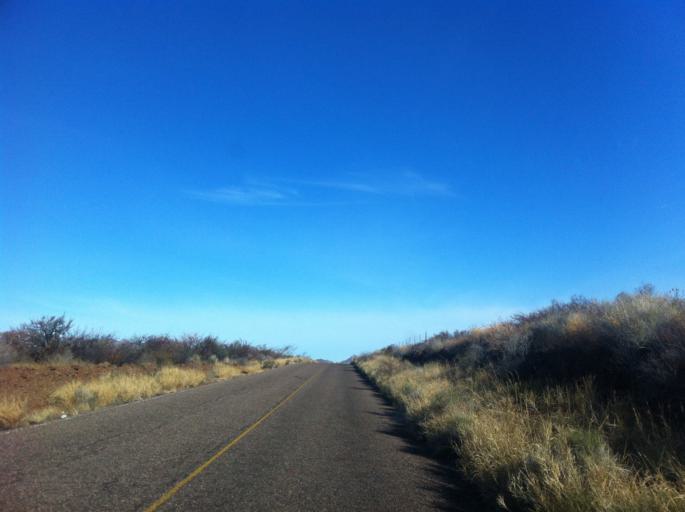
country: MX
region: Sonora
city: Heroica Guaymas
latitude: 27.9322
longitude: -110.9690
